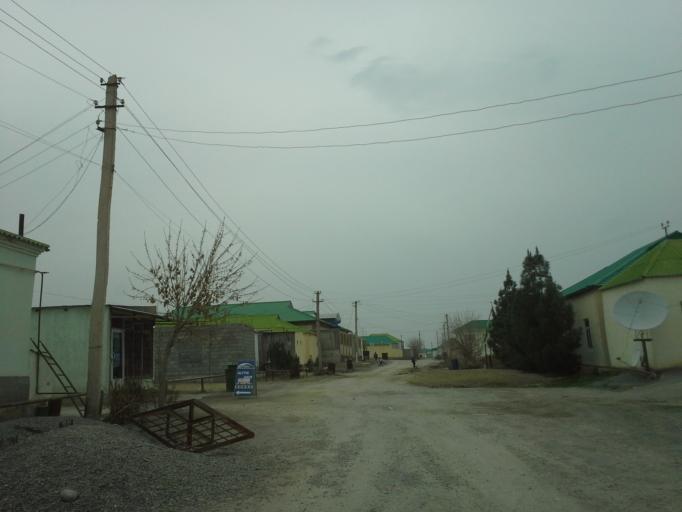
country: TM
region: Ahal
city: Abadan
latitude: 37.9782
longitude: 58.2245
